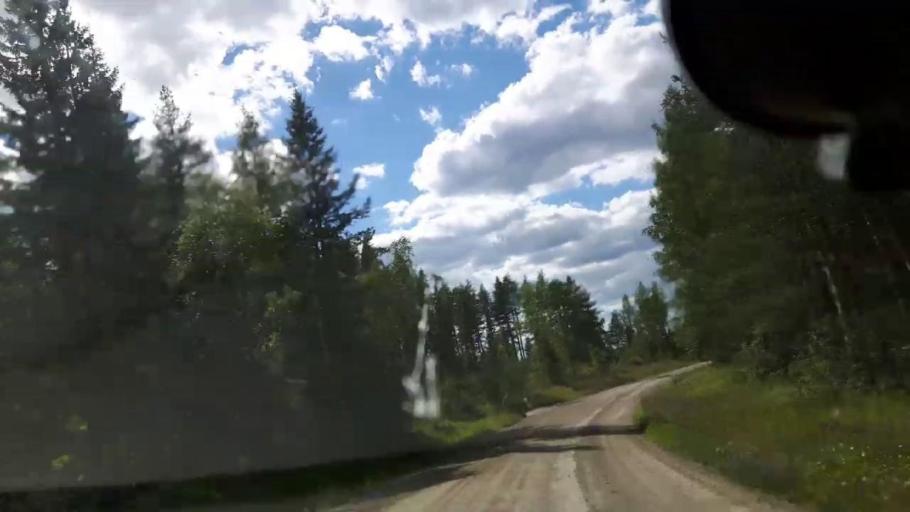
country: SE
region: Jaemtland
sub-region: Braecke Kommun
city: Braecke
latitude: 62.7166
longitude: 15.6087
